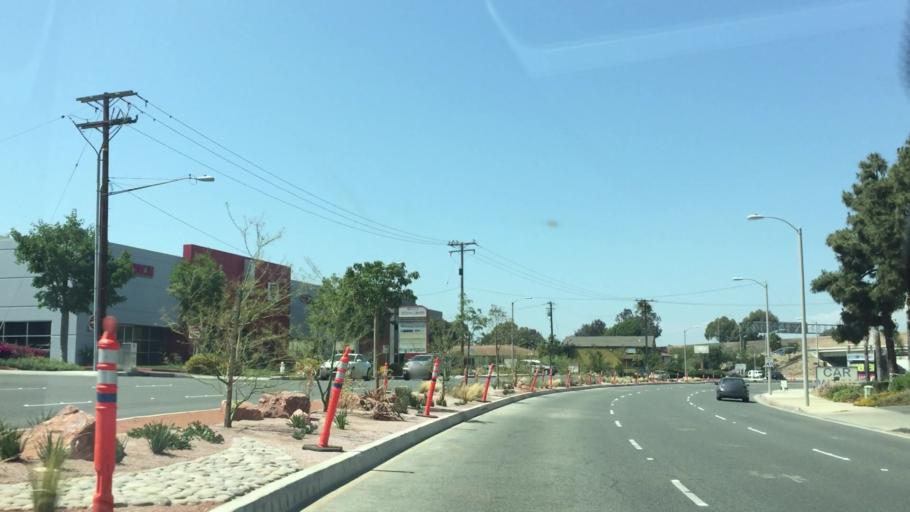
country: US
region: California
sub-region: Orange County
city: Costa Mesa
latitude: 33.6736
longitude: -117.8890
